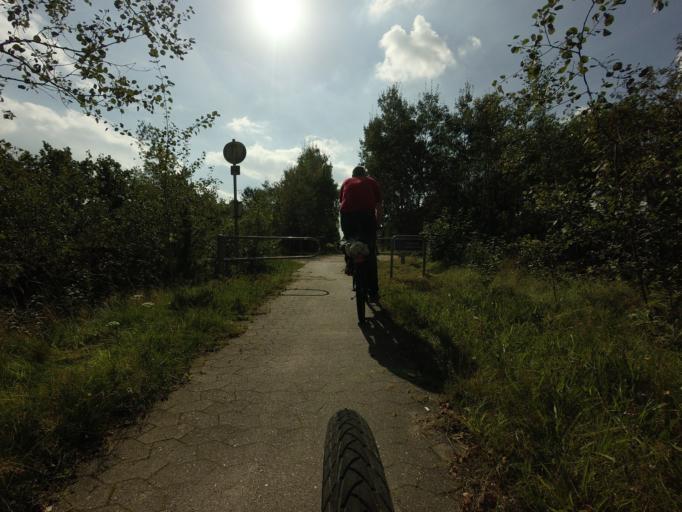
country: DK
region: Central Jutland
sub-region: Viborg Kommune
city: Karup
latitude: 56.2663
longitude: 9.1135
